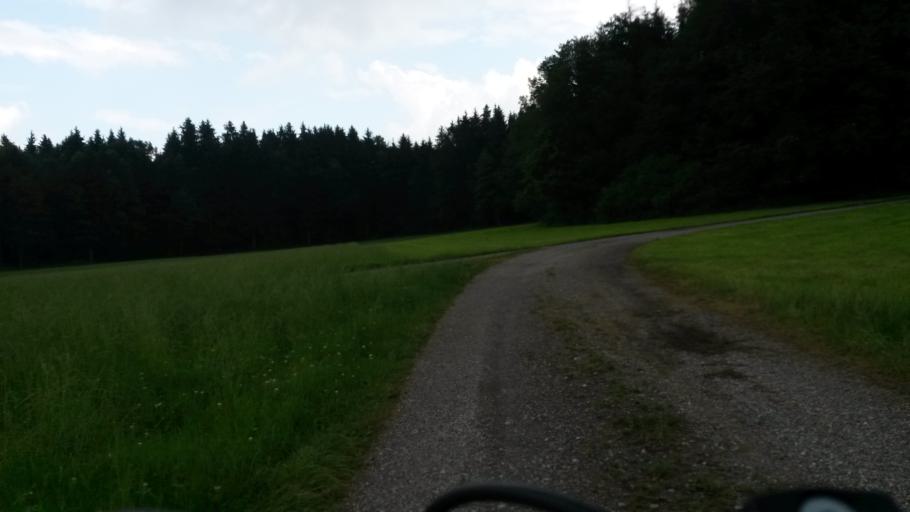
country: DE
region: Bavaria
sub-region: Upper Bavaria
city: Amerang
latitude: 47.9709
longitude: 12.3068
